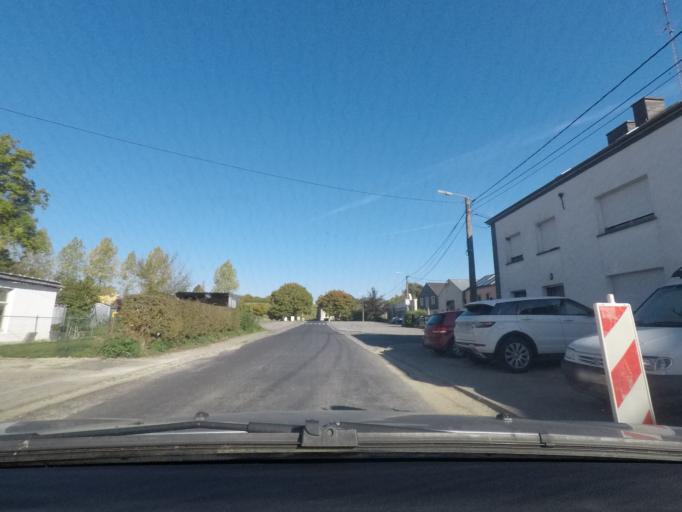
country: BE
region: Wallonia
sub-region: Province du Luxembourg
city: Etalle
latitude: 49.6745
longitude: 5.6001
